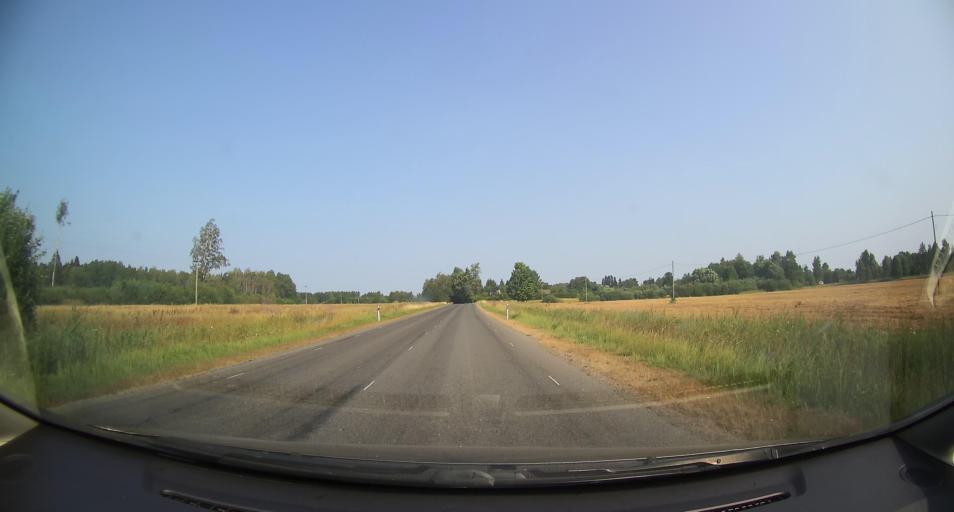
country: EE
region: Paernumaa
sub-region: Audru vald
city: Audru
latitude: 58.4327
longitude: 24.3135
